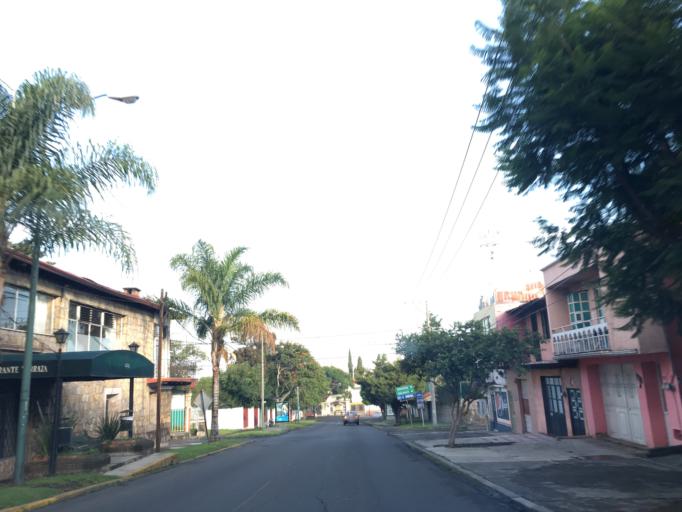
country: MX
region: Michoacan
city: Morelia
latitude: 19.6792
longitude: -101.1962
